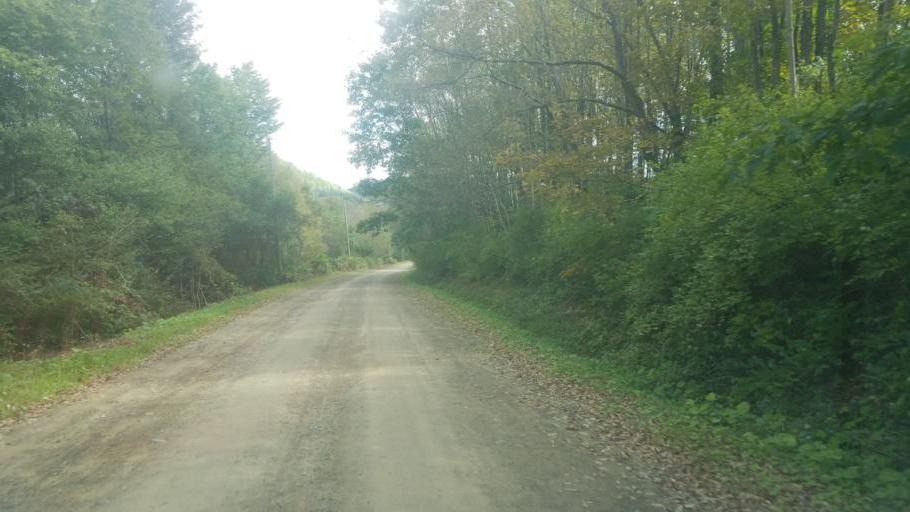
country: US
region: New York
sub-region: Allegany County
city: Cuba
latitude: 42.1496
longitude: -78.2963
